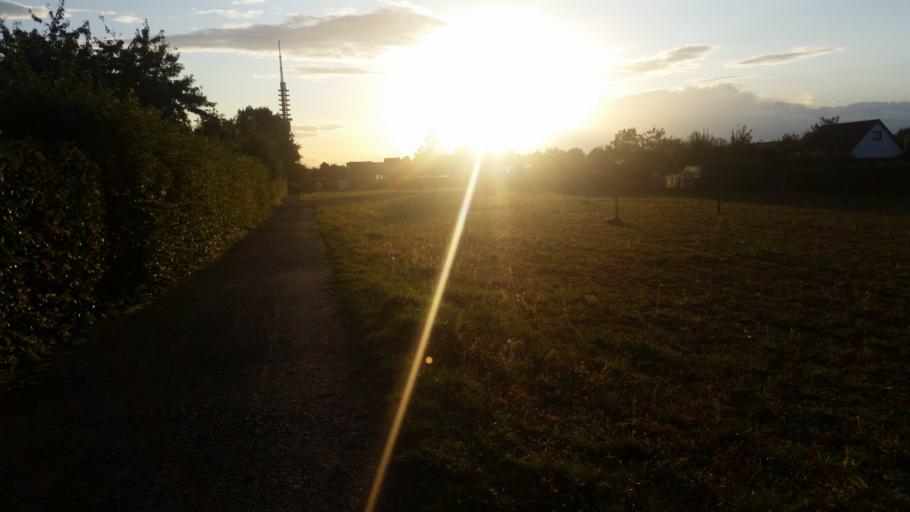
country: DE
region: Lower Saxony
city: Isernhagen Farster Bauerschaft
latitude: 52.3970
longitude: 9.8226
